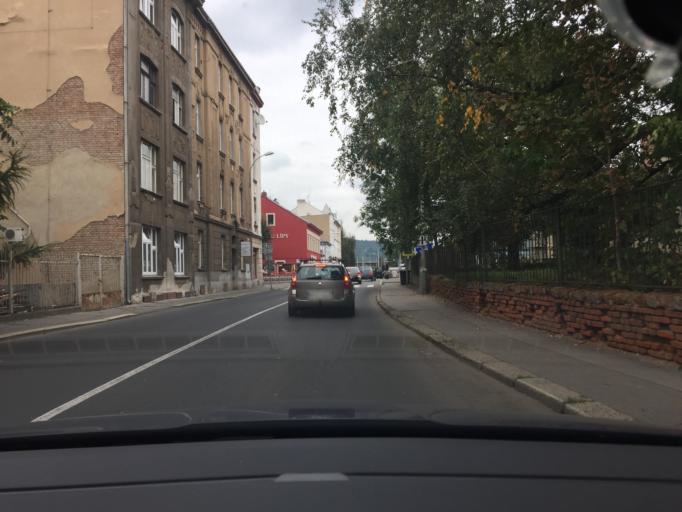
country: CZ
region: Ustecky
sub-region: Okres Usti nad Labem
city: Usti nad Labem
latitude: 50.6554
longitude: 14.0492
